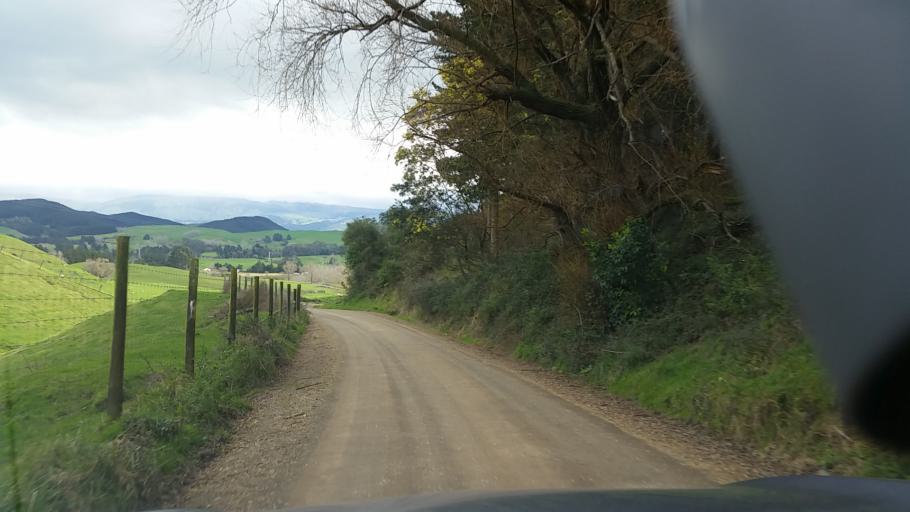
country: NZ
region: Hawke's Bay
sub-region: Napier City
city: Napier
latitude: -39.1909
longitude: 176.9154
